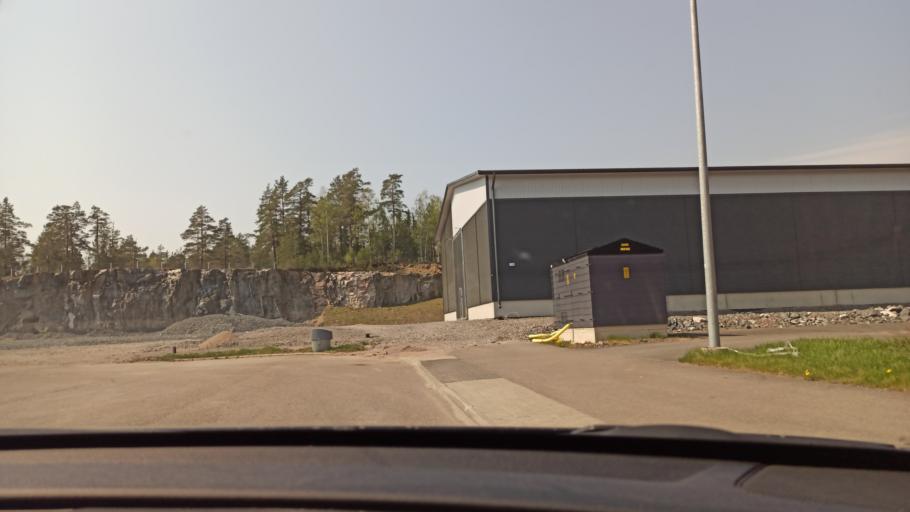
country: FI
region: Uusimaa
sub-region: Helsinki
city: Kirkkonummi
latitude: 60.1263
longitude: 24.5102
